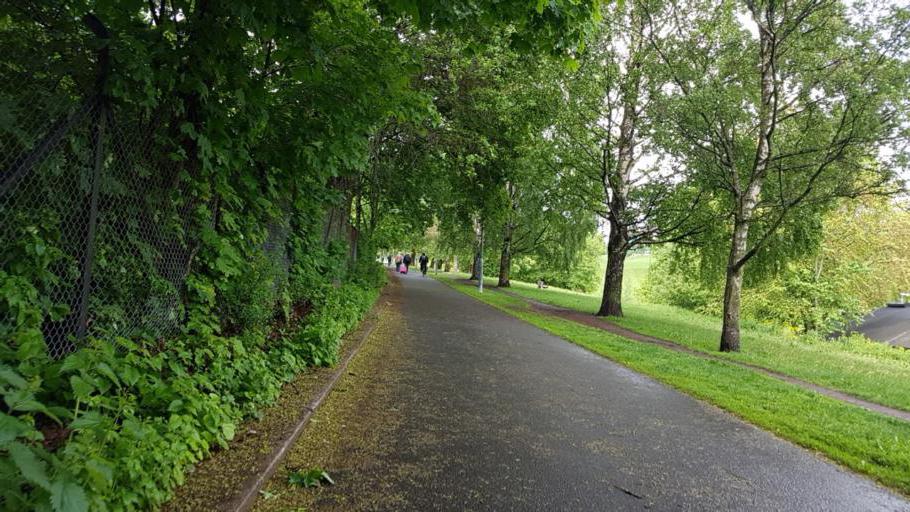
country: NO
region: Oslo
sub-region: Oslo
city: Oslo
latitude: 59.9319
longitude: 10.7730
